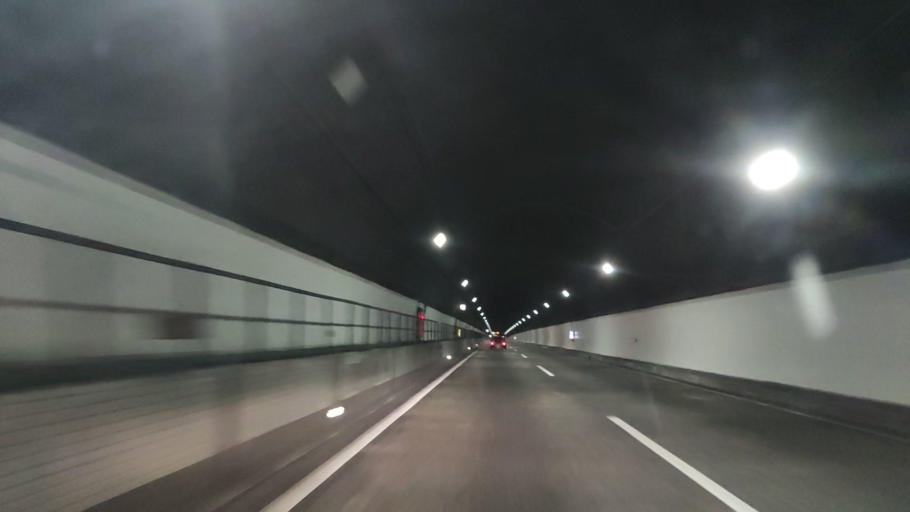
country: JP
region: Okayama
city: Okayama-shi
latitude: 34.7741
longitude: 134.1109
